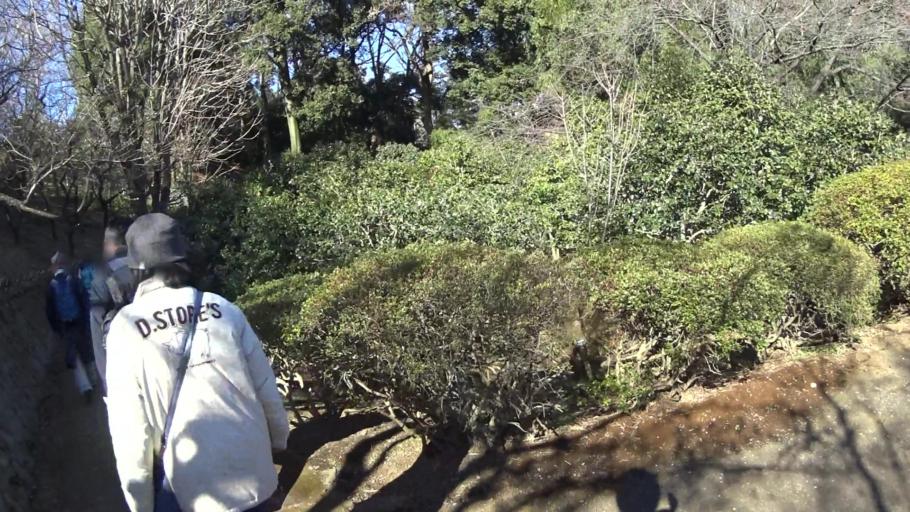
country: JP
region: Saitama
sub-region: Kawaguchi-shi
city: Hatogaya-honcho
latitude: 35.8498
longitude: 139.7554
